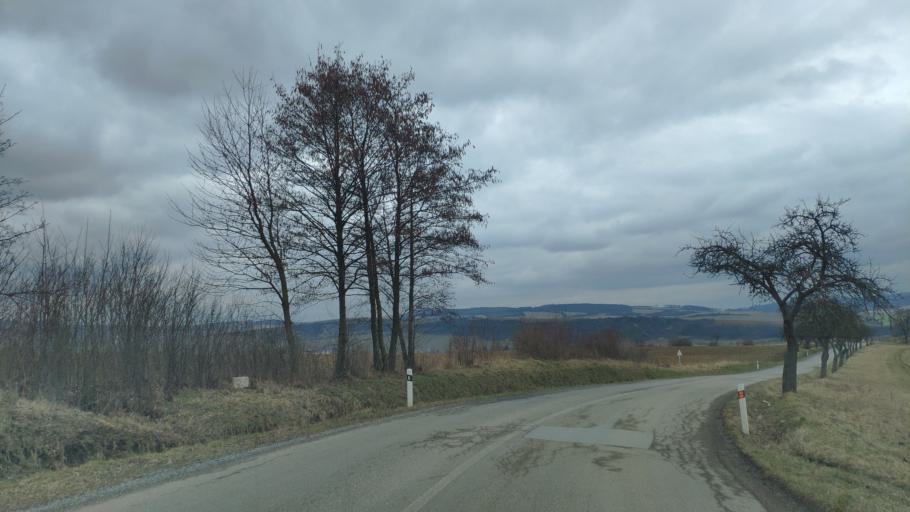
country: SK
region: Presovsky
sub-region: Okres Presov
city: Presov
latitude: 49.0767
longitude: 21.2684
